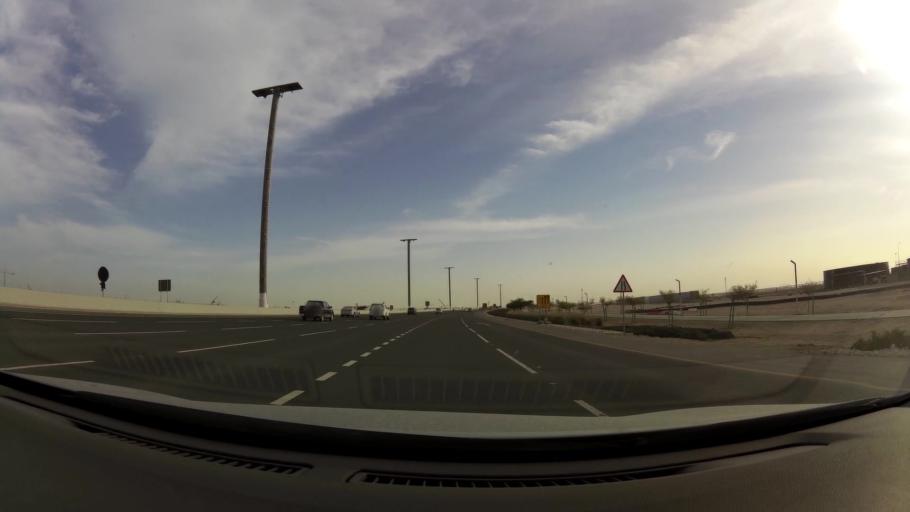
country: QA
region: Al Wakrah
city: Al Wakrah
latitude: 25.2331
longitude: 51.5927
